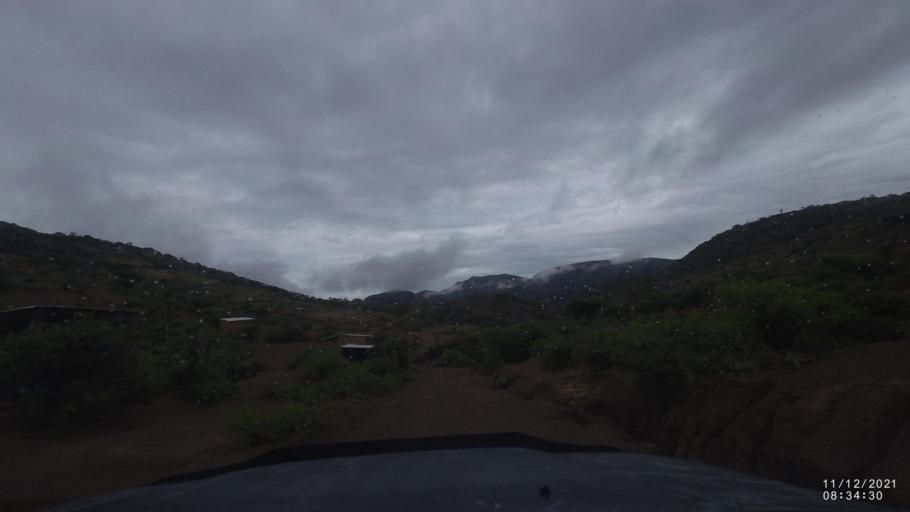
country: BO
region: Cochabamba
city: Tarata
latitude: -17.9323
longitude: -65.9350
